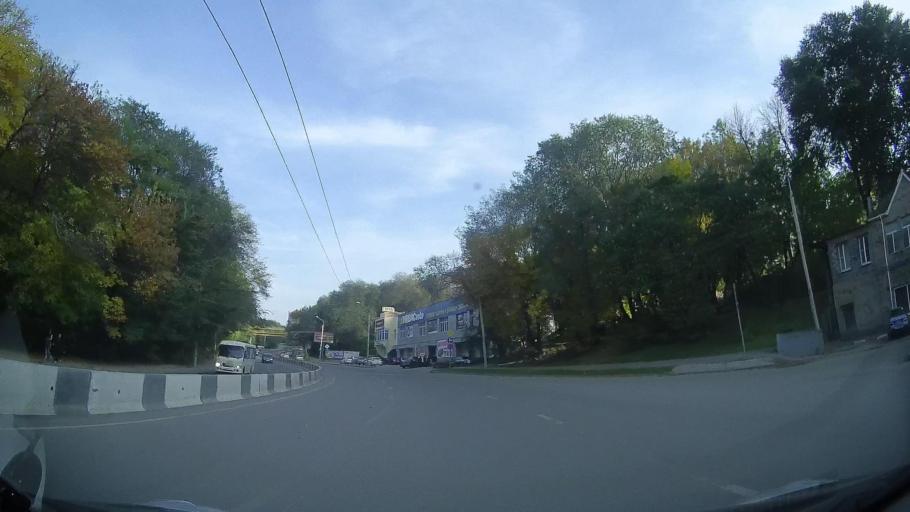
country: RU
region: Rostov
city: Temernik
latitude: 47.2907
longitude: 39.7347
